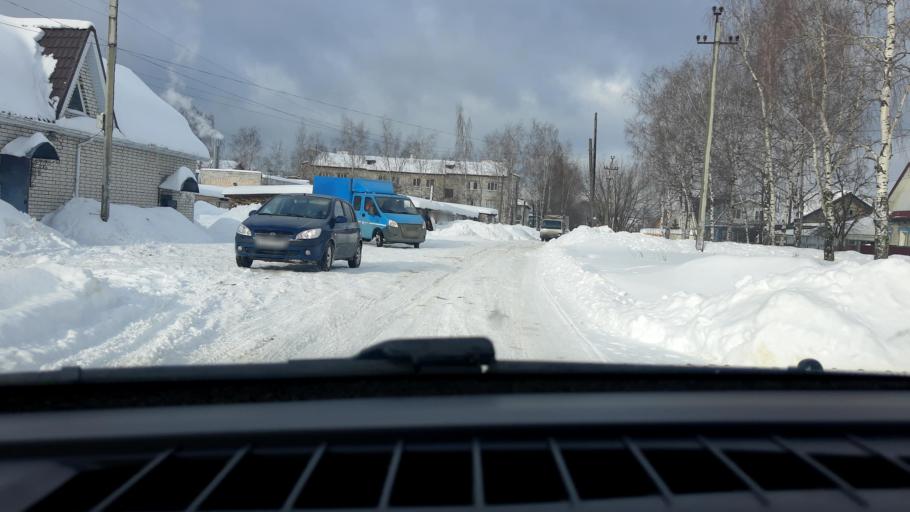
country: RU
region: Nizjnij Novgorod
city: Lukino
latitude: 56.3966
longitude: 43.7057
